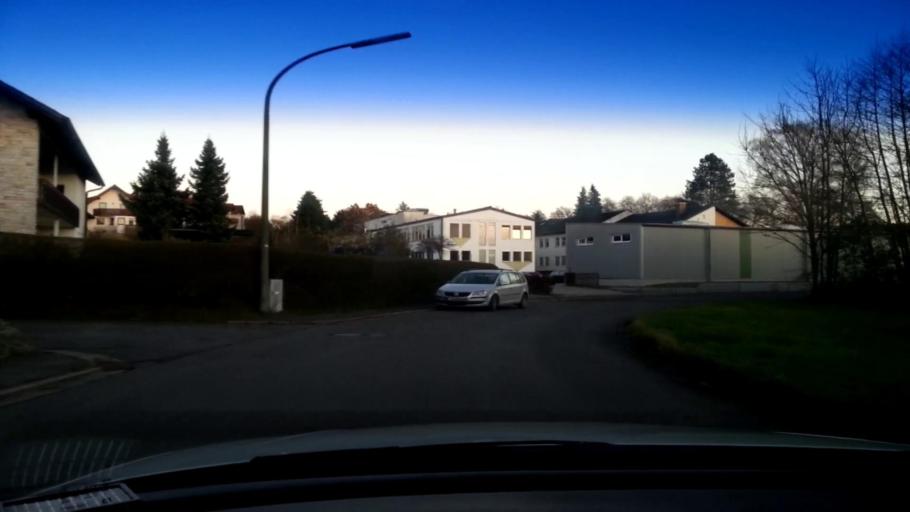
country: DE
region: Bavaria
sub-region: Upper Franconia
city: Zapfendorf
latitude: 50.0181
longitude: 10.9405
